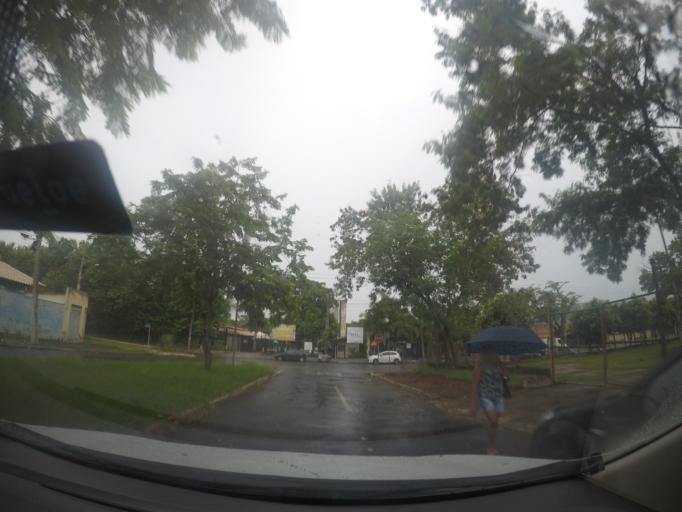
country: BR
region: Goias
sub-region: Goiania
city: Goiania
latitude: -16.6496
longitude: -49.2241
